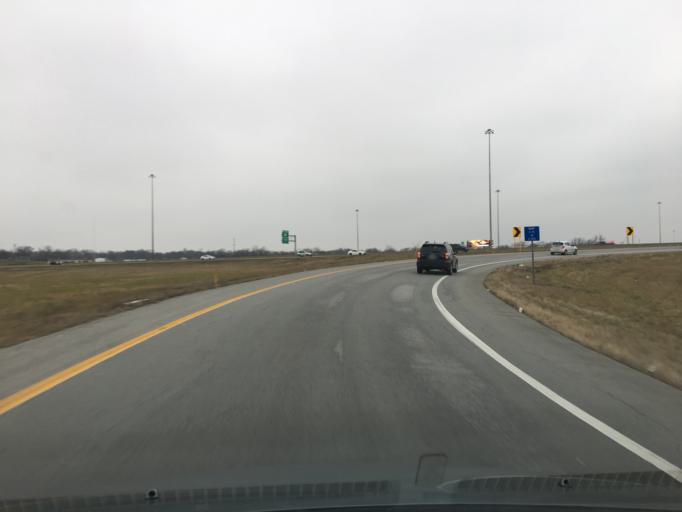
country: US
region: Ohio
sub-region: Hamilton County
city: Glendale
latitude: 39.2894
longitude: -84.4442
